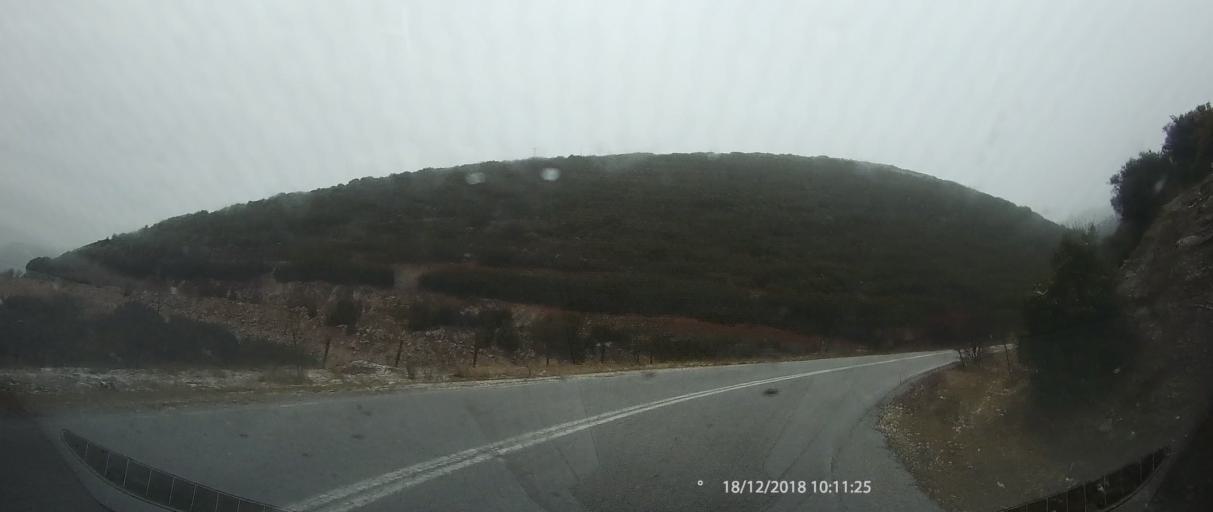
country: GR
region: Thessaly
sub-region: Nomos Larisis
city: Livadi
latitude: 40.0927
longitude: 22.2103
